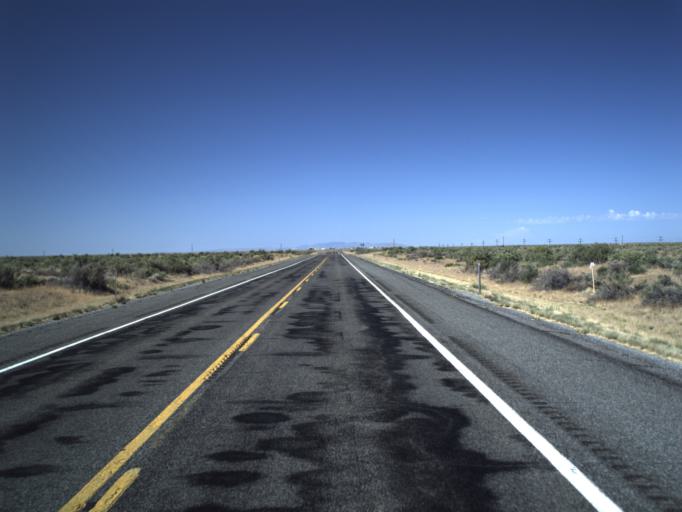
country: US
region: Utah
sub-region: Millard County
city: Delta
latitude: 39.4173
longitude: -112.4805
